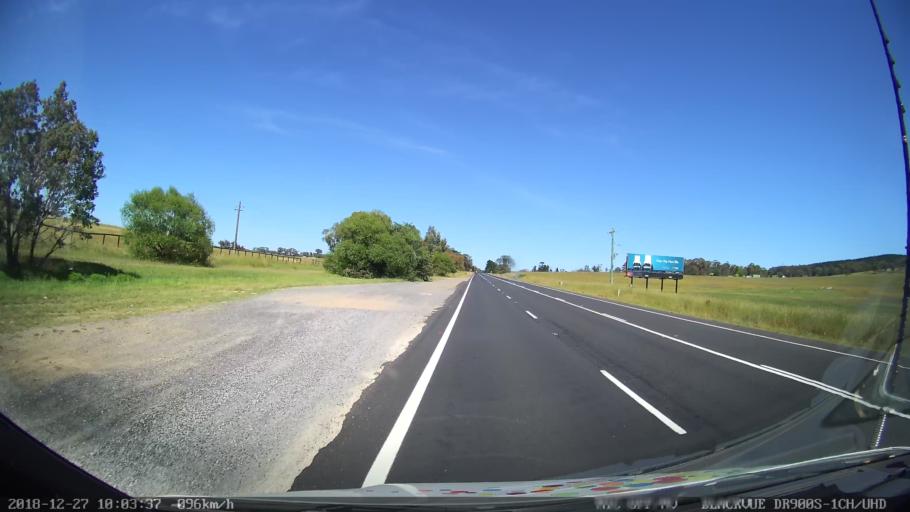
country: AU
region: New South Wales
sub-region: Lithgow
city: Portland
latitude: -33.4332
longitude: 149.9023
